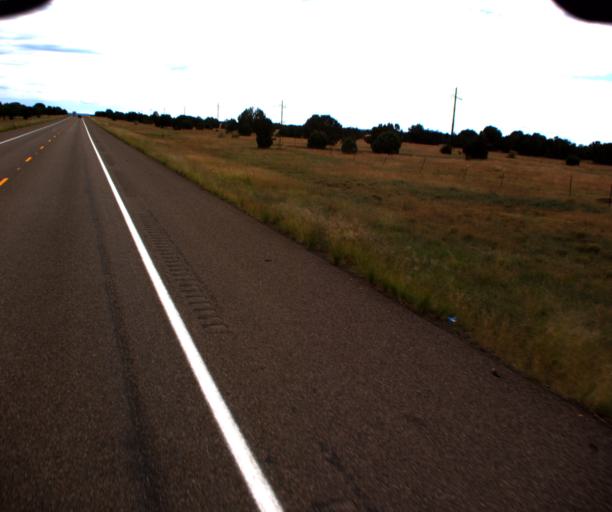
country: US
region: Arizona
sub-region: Navajo County
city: Show Low
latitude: 34.3015
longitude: -110.0354
